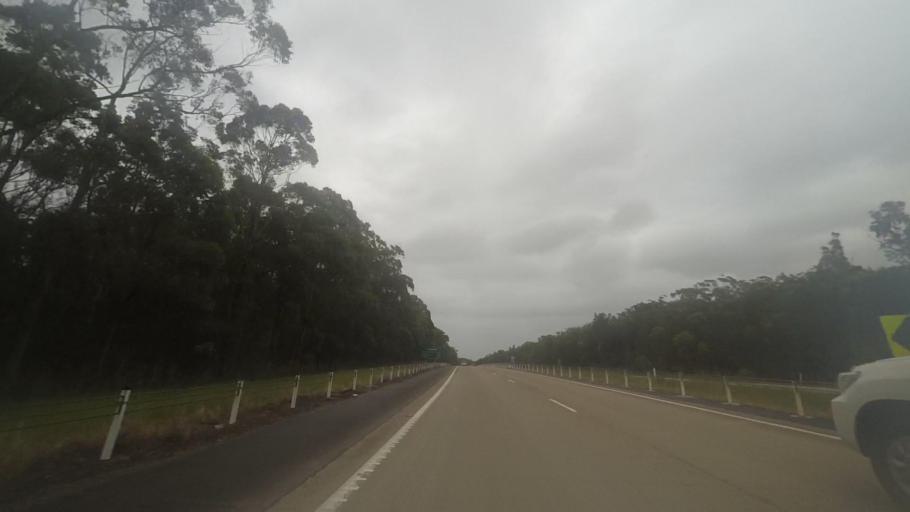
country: AU
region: New South Wales
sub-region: Port Stephens Shire
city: Medowie
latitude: -32.6506
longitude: 151.9018
